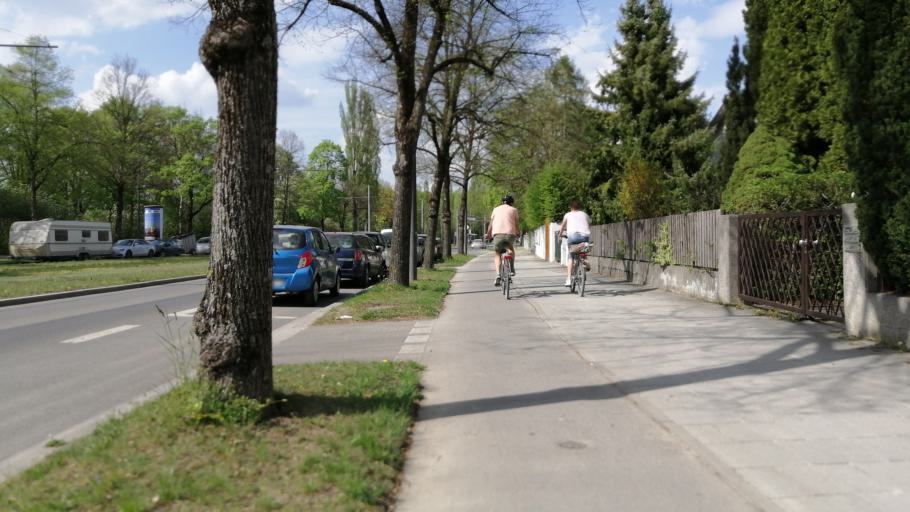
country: DE
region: Bavaria
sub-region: Upper Bavaria
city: Bogenhausen
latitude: 48.1571
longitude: 11.6295
